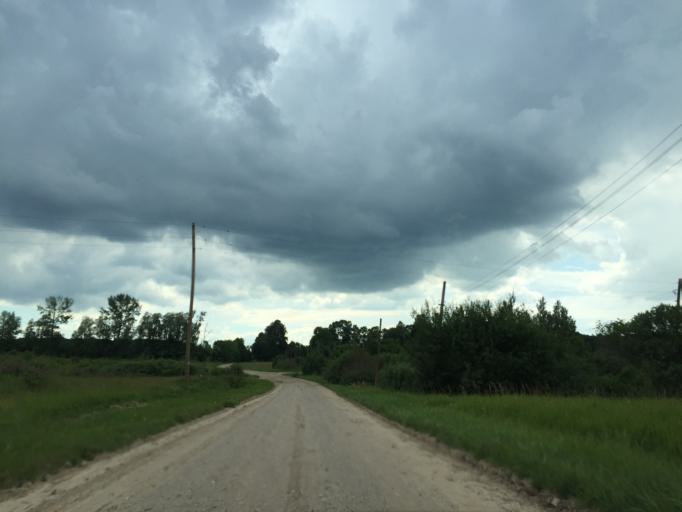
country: LV
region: Ligatne
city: Ligatne
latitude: 57.2211
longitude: 25.0326
